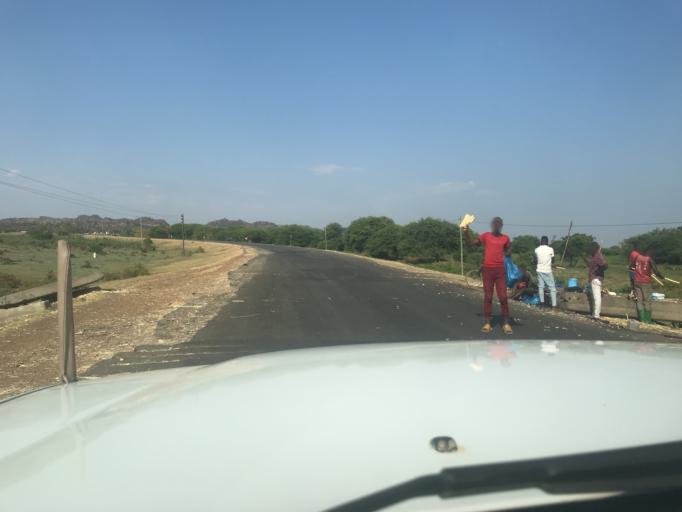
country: TZ
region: Mwanza
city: Kihangara
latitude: -2.5754
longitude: 33.4608
